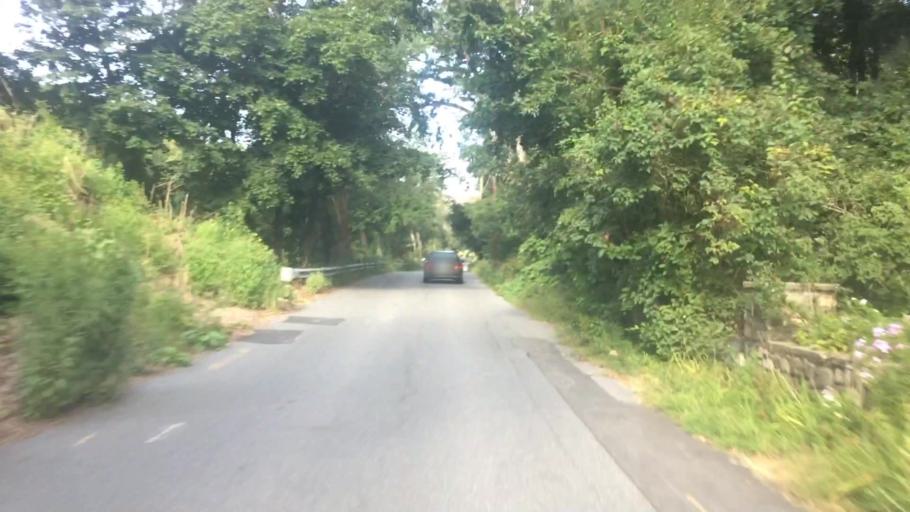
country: US
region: Massachusetts
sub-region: Middlesex County
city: Maynard
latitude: 42.4599
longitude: -71.4444
